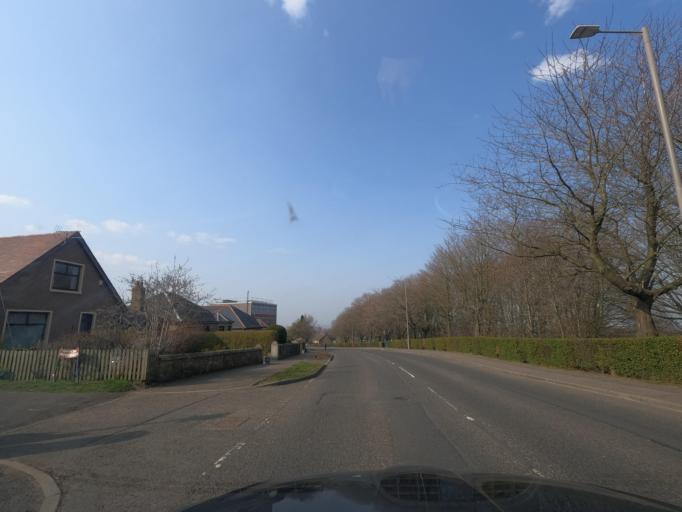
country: GB
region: Scotland
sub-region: Falkirk
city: Polmont
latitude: 55.9795
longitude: -3.7165
